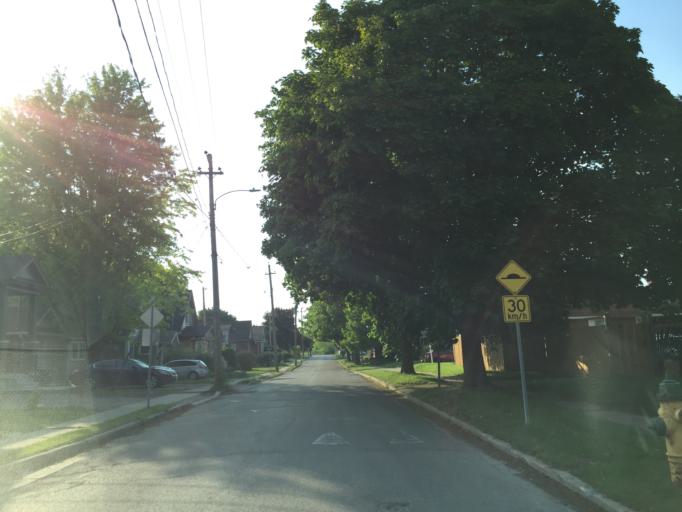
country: CA
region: Ontario
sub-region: Wellington County
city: Guelph
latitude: 43.5554
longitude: -80.2688
